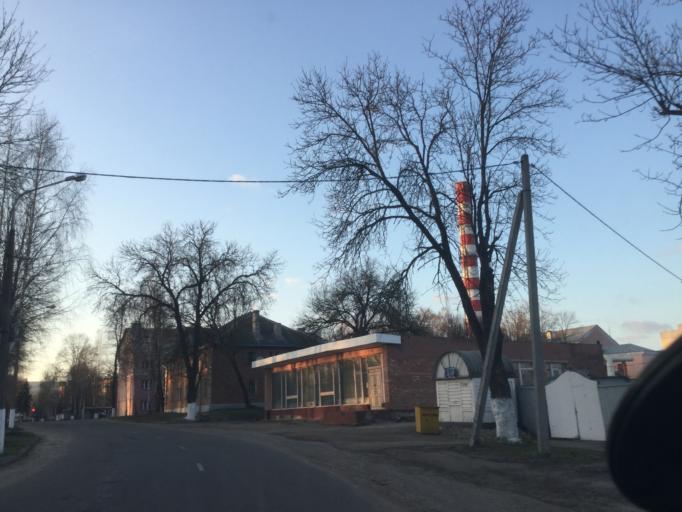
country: BY
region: Vitebsk
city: Vitebsk
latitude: 55.1653
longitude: 30.1309
